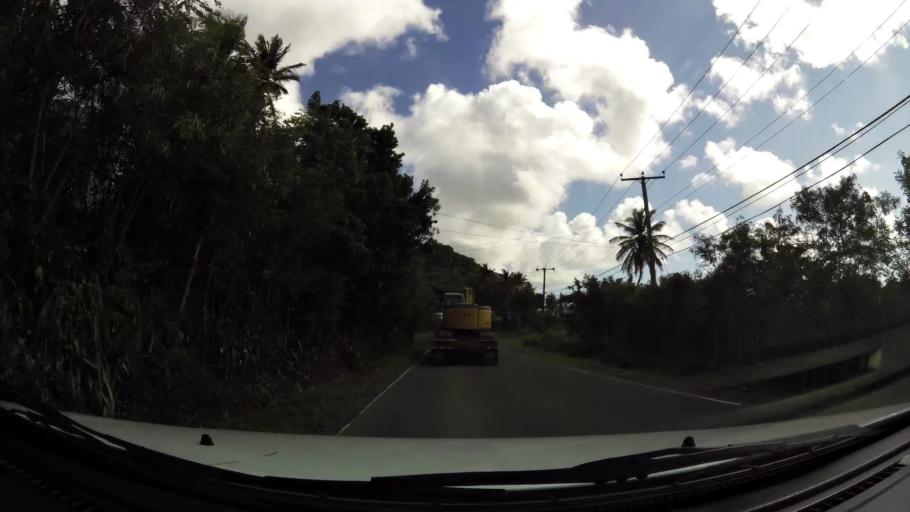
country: LC
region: Laborie Quarter
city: Laborie
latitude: 13.7524
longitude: -61.0058
